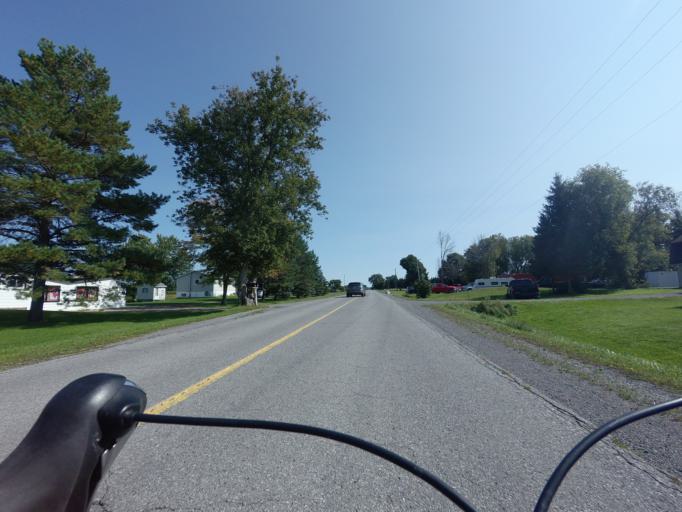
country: CA
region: Ontario
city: Carleton Place
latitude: 45.3456
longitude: -76.1069
